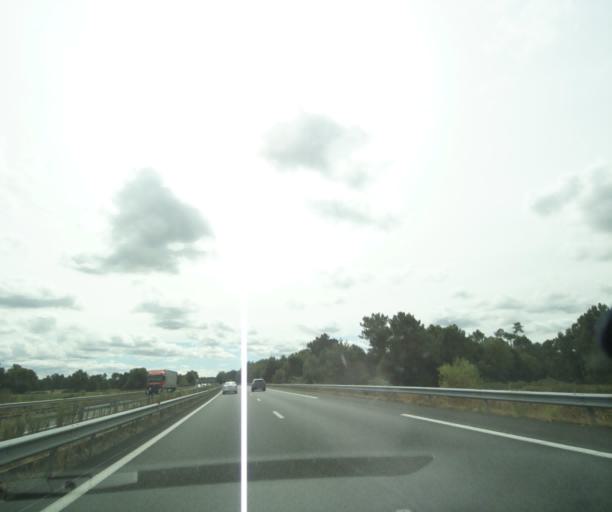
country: FR
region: Aquitaine
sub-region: Departement de la Gironde
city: Reignac
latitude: 45.2096
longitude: -0.5037
